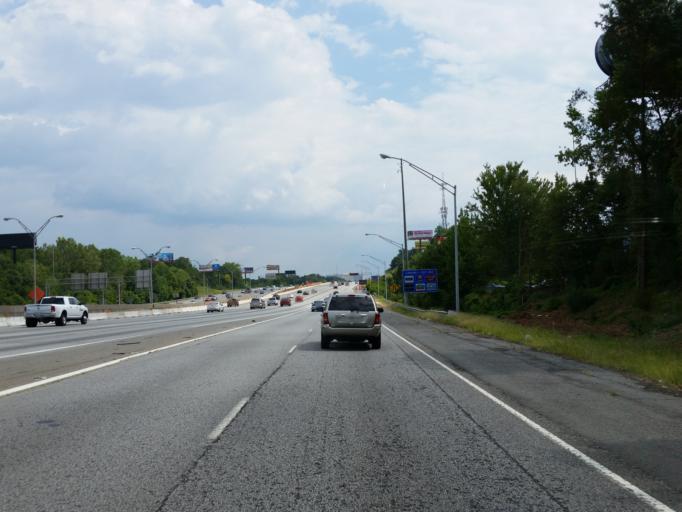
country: US
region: Georgia
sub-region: Cobb County
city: Smyrna
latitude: 33.9209
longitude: -84.4848
